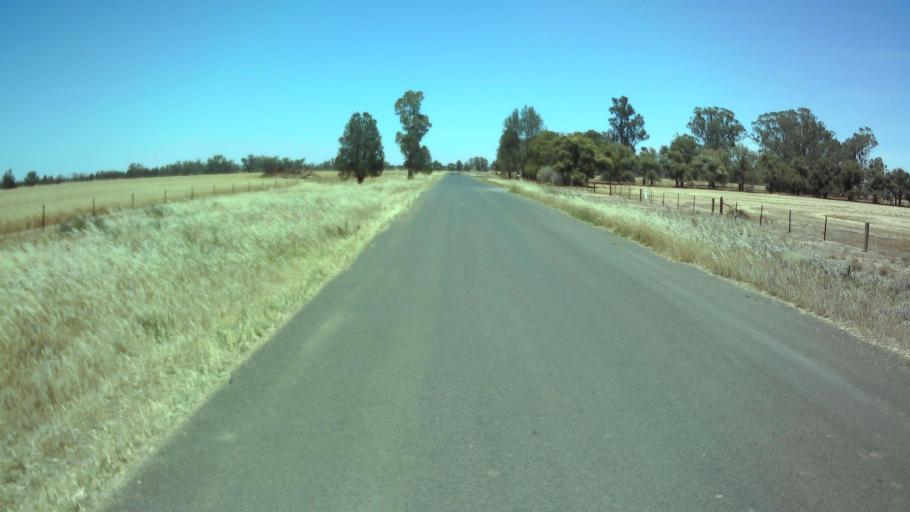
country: AU
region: New South Wales
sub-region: Weddin
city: Grenfell
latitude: -34.0305
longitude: 147.7907
